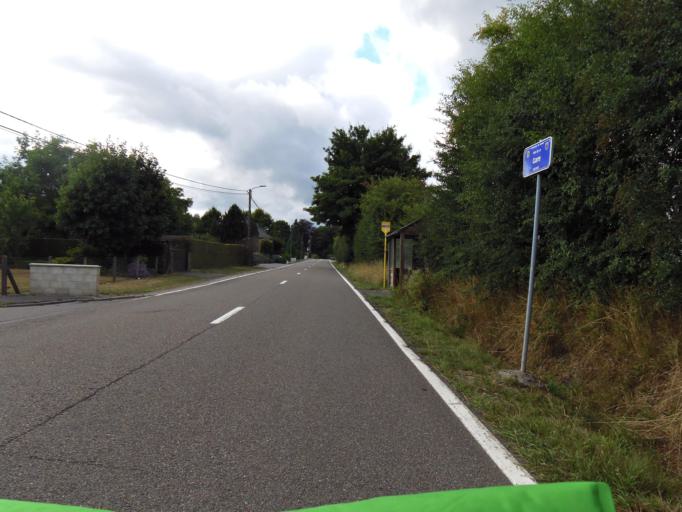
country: BE
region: Wallonia
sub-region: Province de Namur
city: Bievre
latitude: 49.9371
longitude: 5.0277
